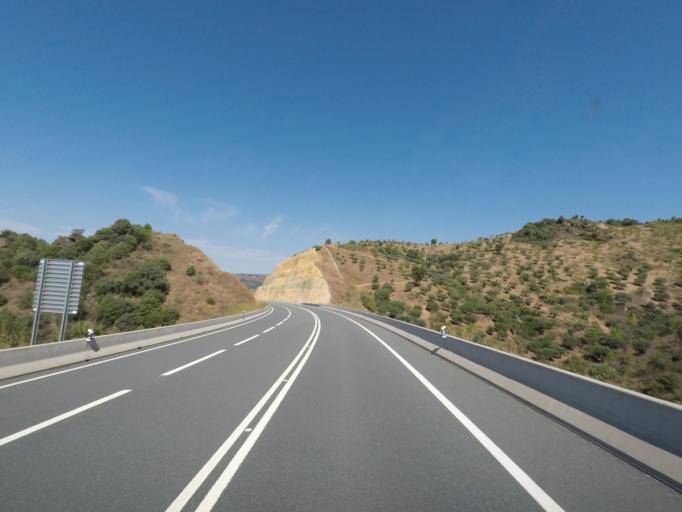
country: PT
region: Braganca
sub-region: Alfandega da Fe
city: Alfandega da Fe
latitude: 41.2948
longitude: -6.8963
